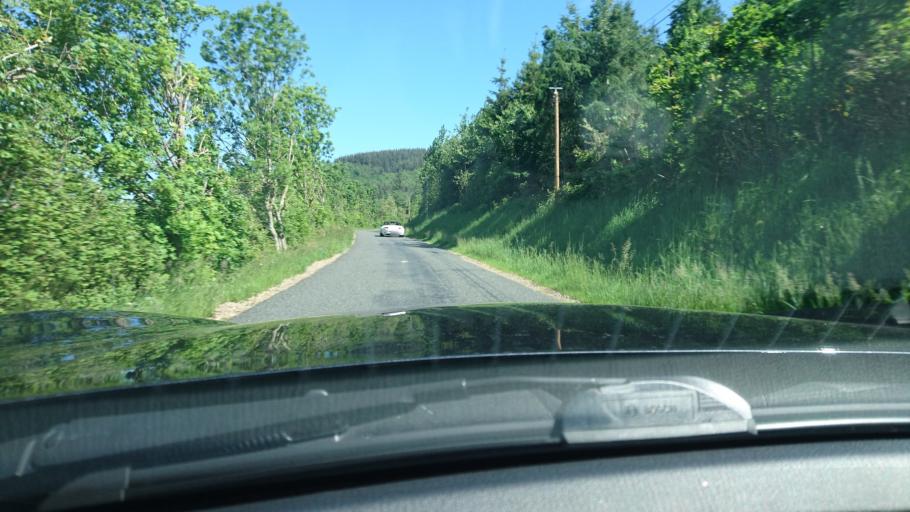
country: FR
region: Rhone-Alpes
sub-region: Departement de la Loire
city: Violay
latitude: 45.8367
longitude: 4.3706
